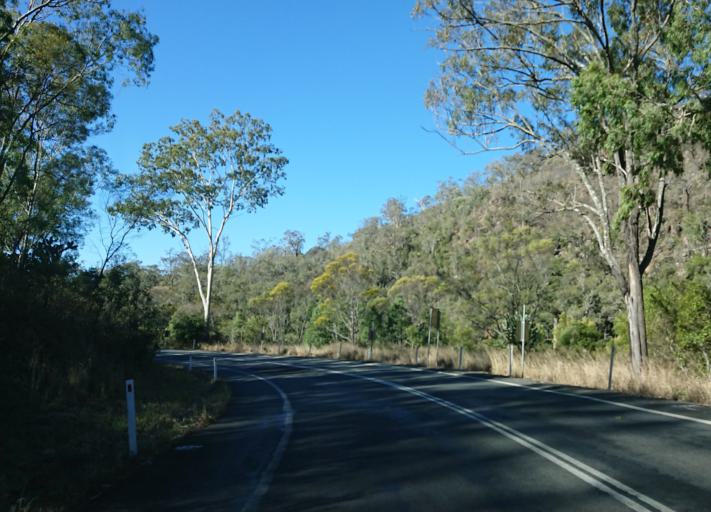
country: AU
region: Queensland
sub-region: Toowoomba
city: Top Camp
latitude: -27.7461
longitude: 152.0921
